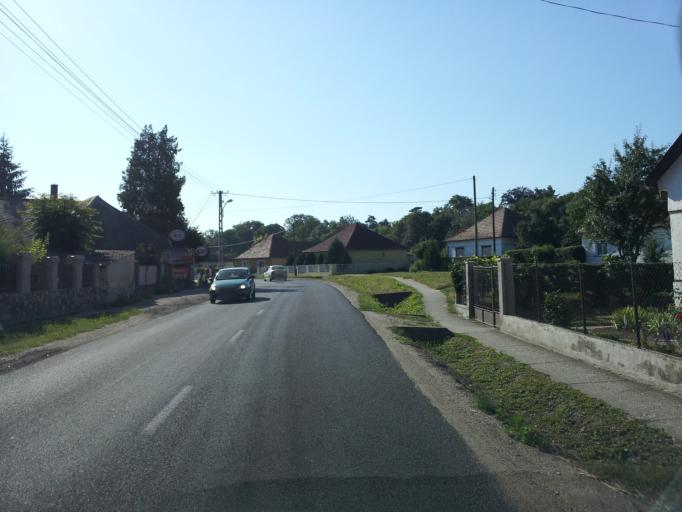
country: HU
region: Veszprem
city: Osi
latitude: 47.1370
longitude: 18.2412
